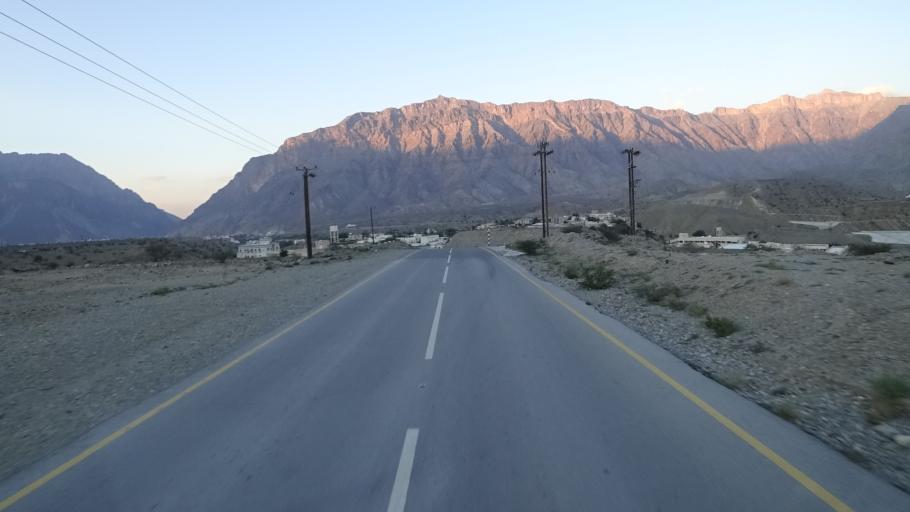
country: OM
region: Al Batinah
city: Rustaq
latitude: 23.2821
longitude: 57.3292
